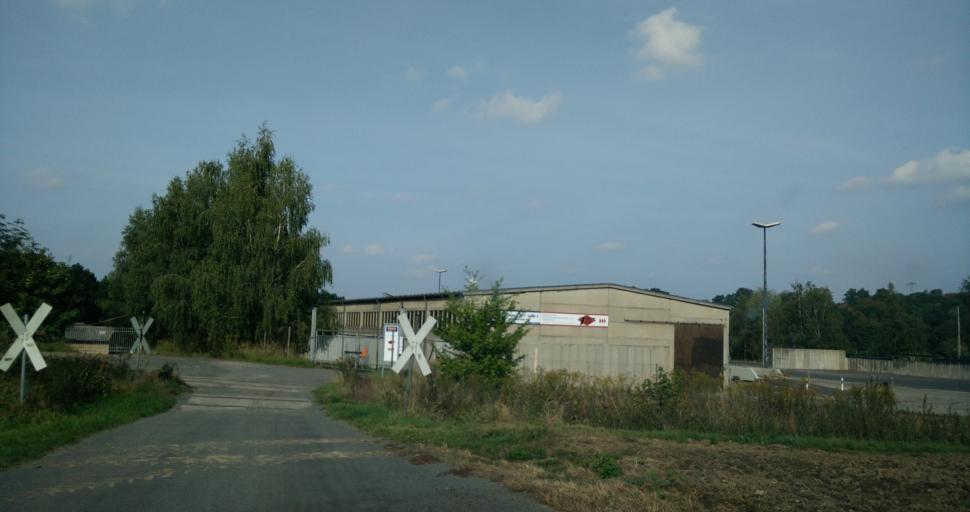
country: DE
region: Saxony
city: Colditz
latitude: 51.1435
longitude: 12.7932
